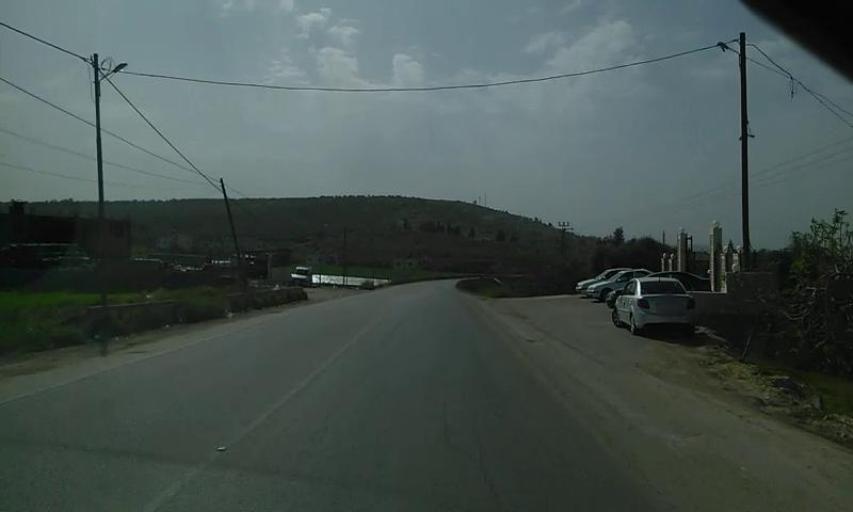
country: PS
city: Bir al Basha
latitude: 32.4250
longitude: 35.2493
